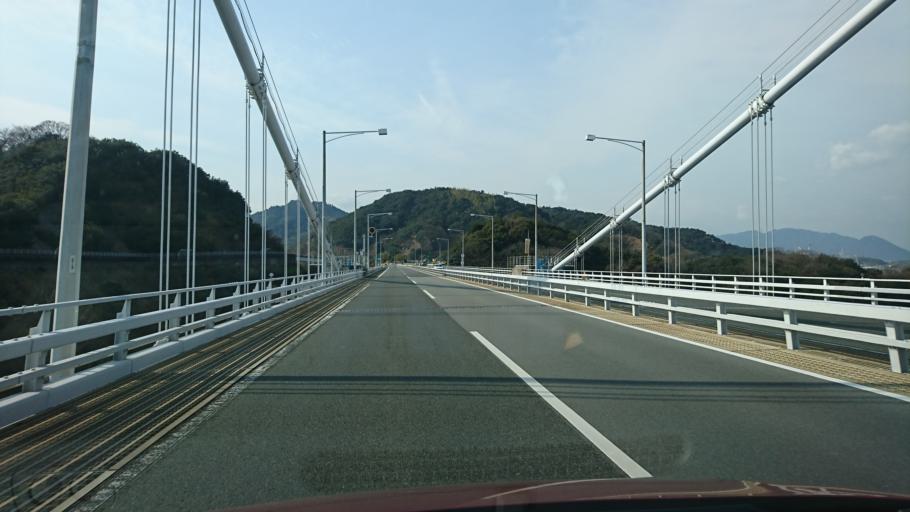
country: JP
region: Hiroshima
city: Onomichi
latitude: 34.3548
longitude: 133.1749
